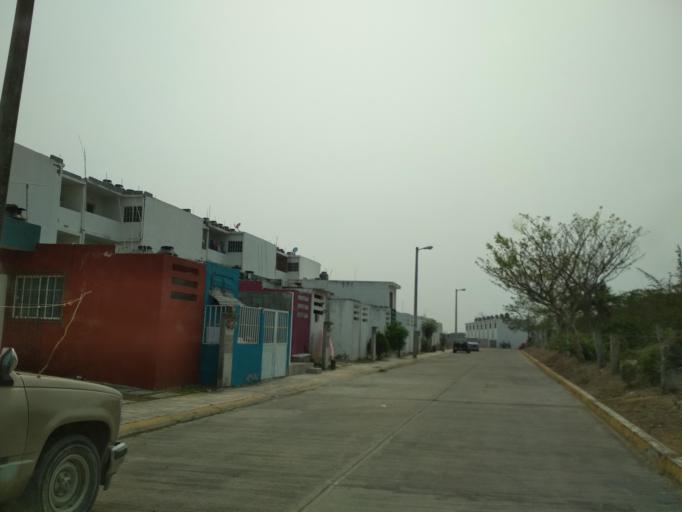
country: MX
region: Veracruz
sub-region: Veracruz
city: Las Amapolas
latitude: 19.1401
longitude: -96.2192
